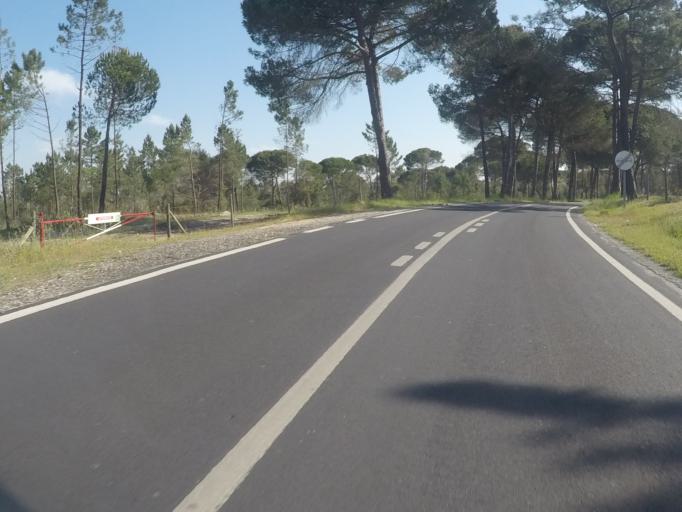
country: PT
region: Setubal
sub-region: Seixal
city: Arrentela
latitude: 38.5436
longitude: -9.1110
